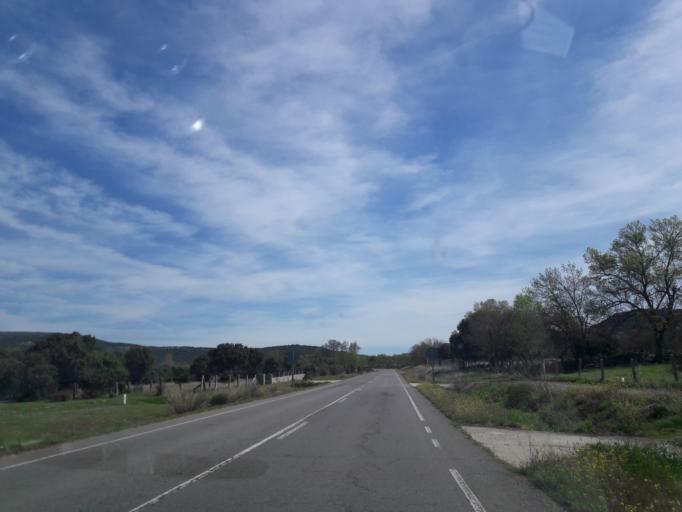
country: ES
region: Castille and Leon
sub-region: Provincia de Salamanca
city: Ledrada
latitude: 40.4847
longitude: -5.7257
